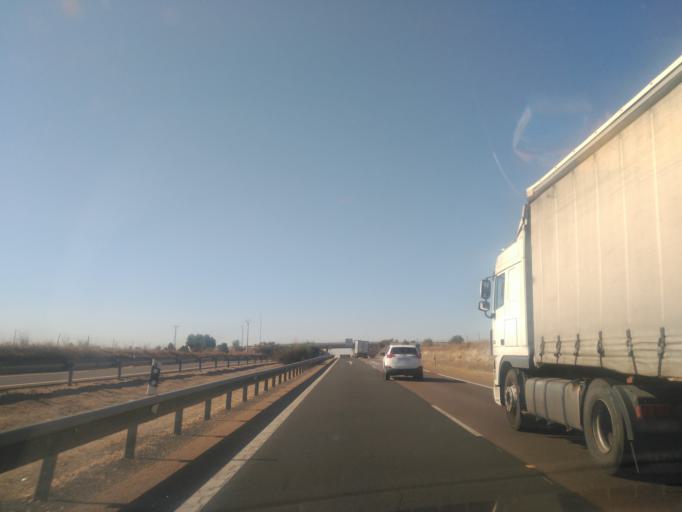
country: ES
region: Castille and Leon
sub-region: Provincia de Valladolid
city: Geria
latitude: 41.5619
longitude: -4.8668
